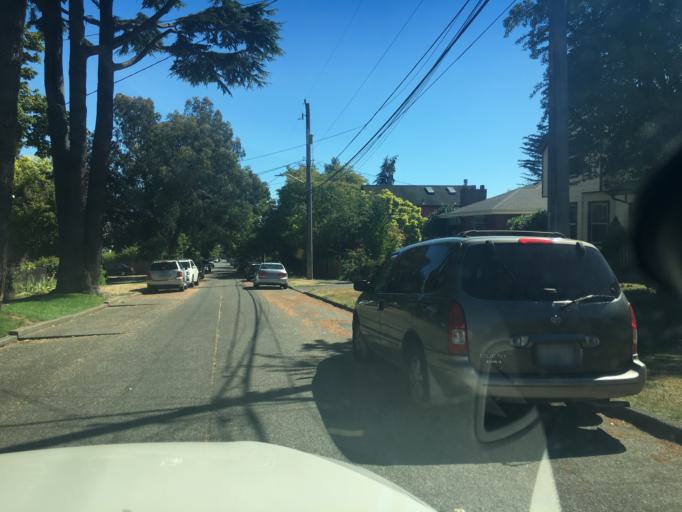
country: US
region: Washington
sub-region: King County
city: Shoreline
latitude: 47.6830
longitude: -122.3898
